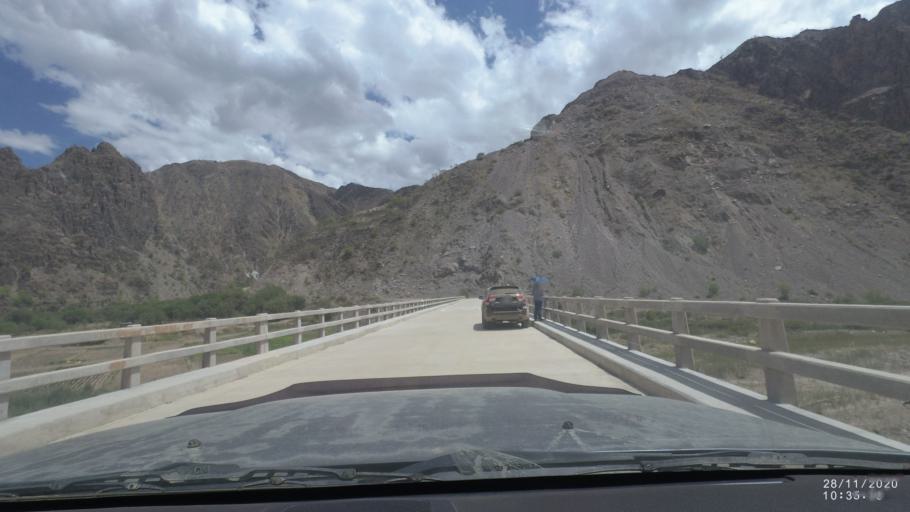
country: BO
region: Cochabamba
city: Capinota
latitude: -17.7947
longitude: -66.1377
